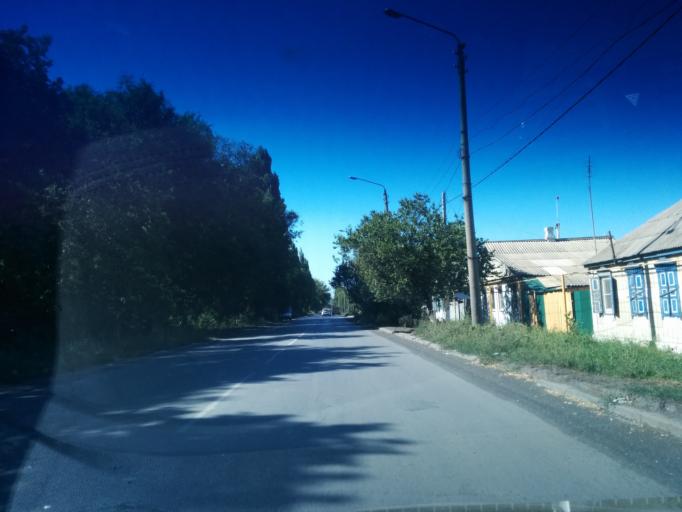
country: RU
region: Rostov
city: Shakhty
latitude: 47.6799
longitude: 40.2818
